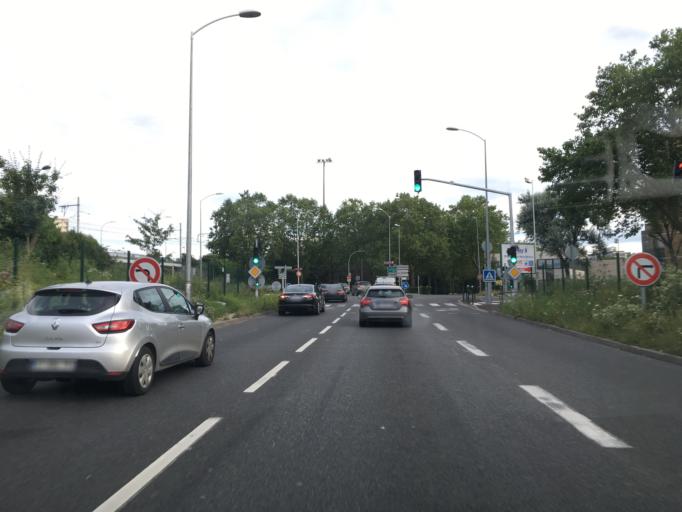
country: FR
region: Ile-de-France
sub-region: Departement du Val-de-Marne
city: Boissy-Saint-Leger
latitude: 48.7556
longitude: 2.5052
